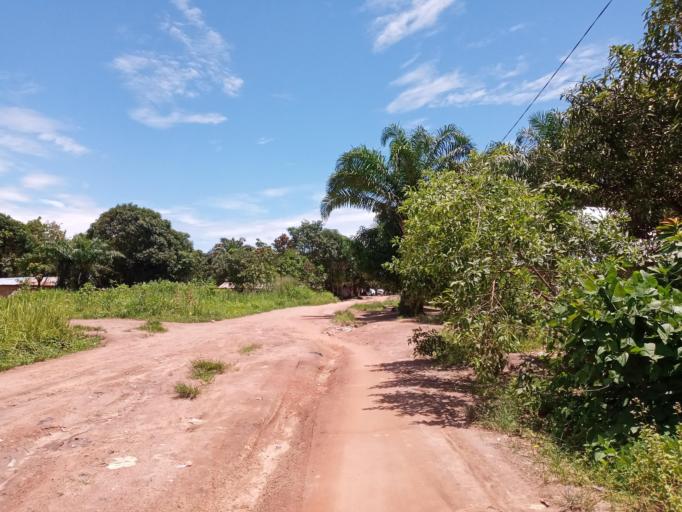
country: SL
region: Eastern Province
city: Koidu
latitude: 8.6337
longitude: -10.9561
